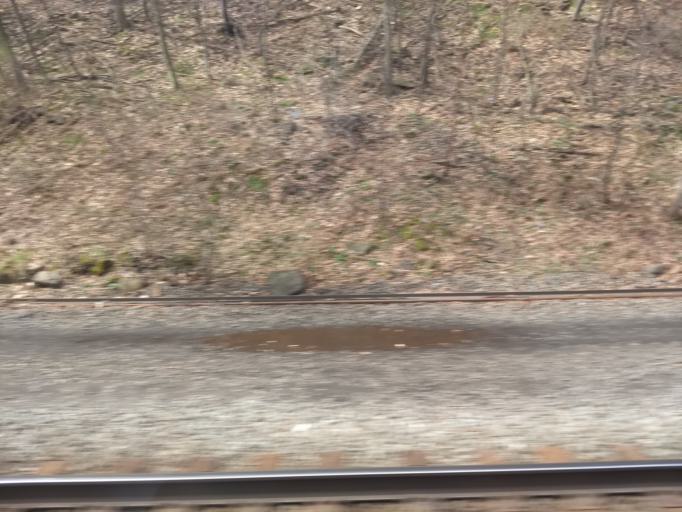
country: US
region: Pennsylvania
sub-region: Blair County
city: Tyrone
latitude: 40.6675
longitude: -78.2333
